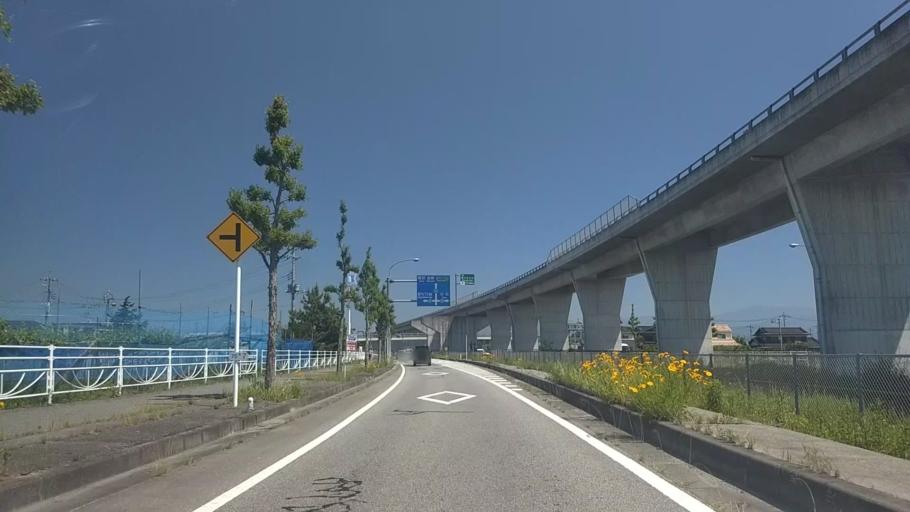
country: JP
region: Yamanashi
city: Ryuo
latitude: 35.6068
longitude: 138.4813
